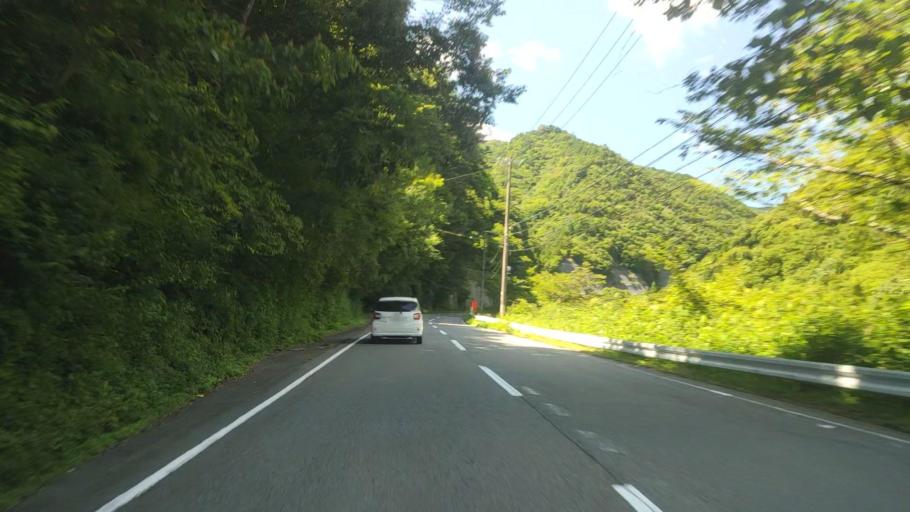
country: JP
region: Nara
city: Yoshino-cho
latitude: 34.2015
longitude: 135.9990
